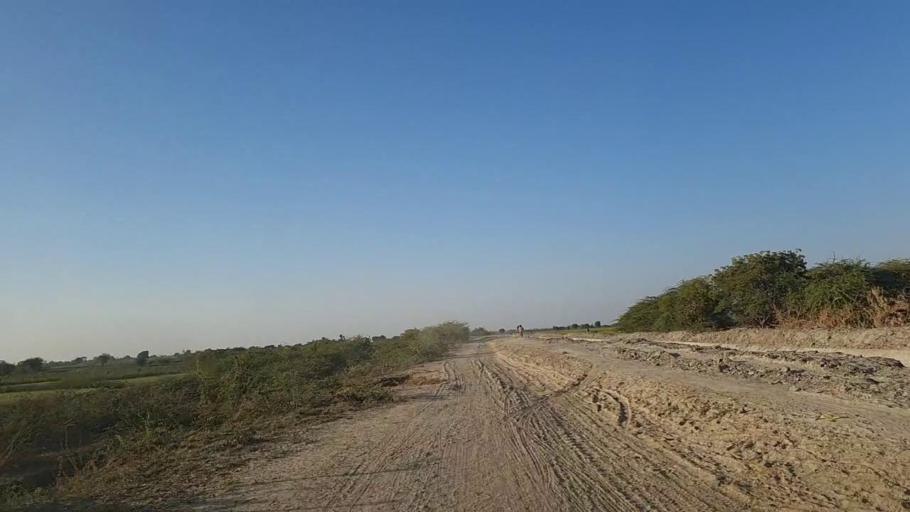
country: PK
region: Sindh
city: Naukot
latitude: 24.9974
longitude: 69.3993
